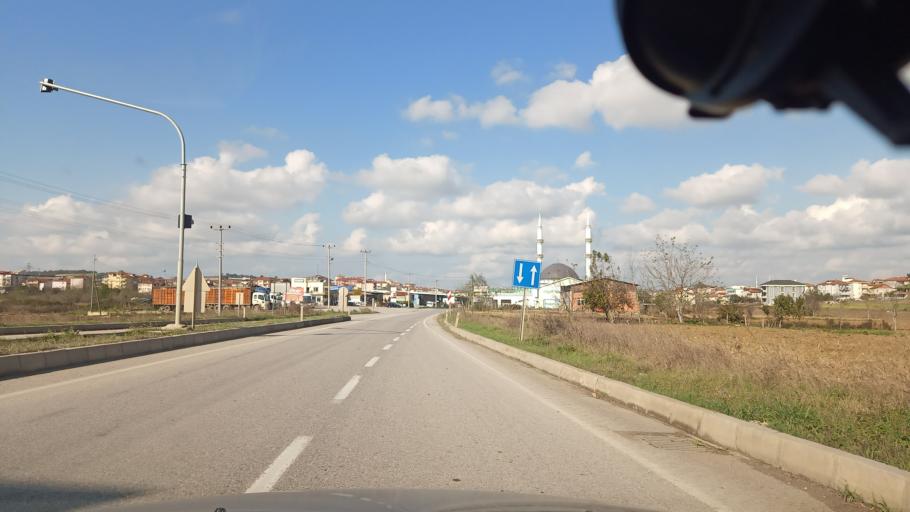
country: TR
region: Sakarya
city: Kaynarca
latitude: 41.0247
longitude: 30.3104
